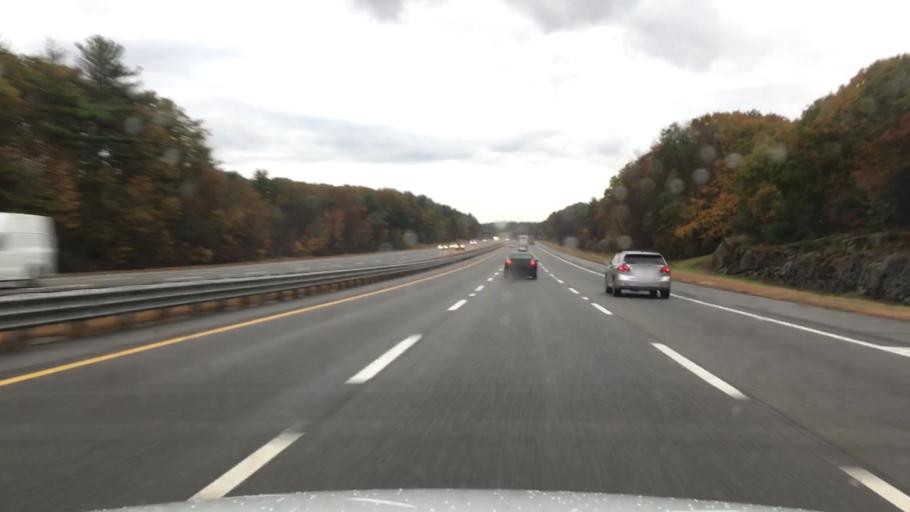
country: US
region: Maine
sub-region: York County
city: Cape Neddick
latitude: 43.2124
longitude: -70.6409
